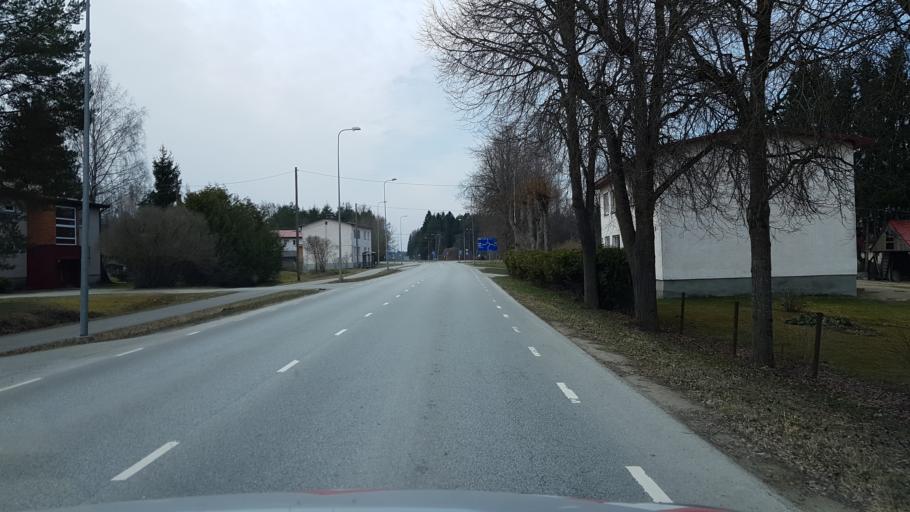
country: EE
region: Ida-Virumaa
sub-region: Aseri vald
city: Aseri
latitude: 59.3511
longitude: 26.8249
